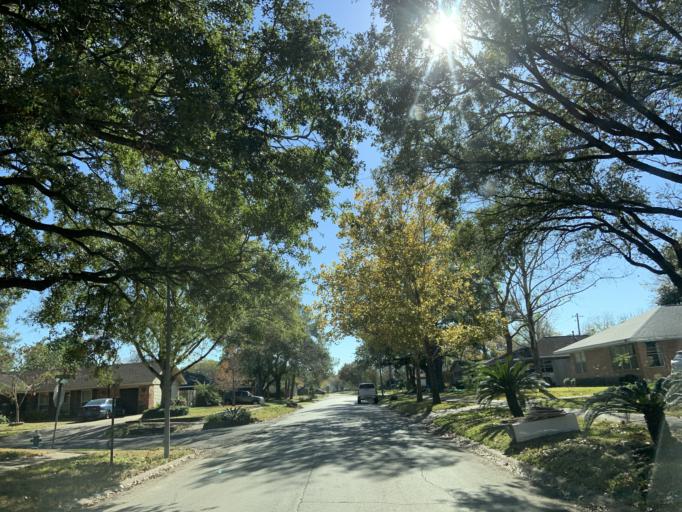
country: US
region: Texas
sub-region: Harris County
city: Bellaire
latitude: 29.6829
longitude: -95.5027
